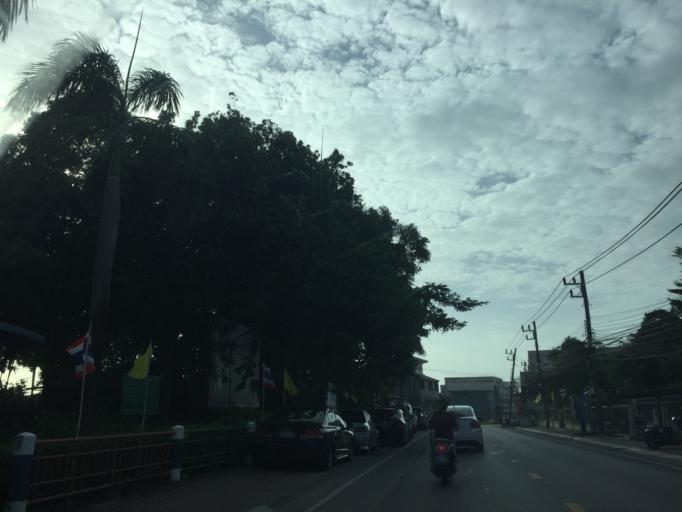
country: TH
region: Phuket
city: Mueang Phuket
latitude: 7.8614
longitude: 98.3735
